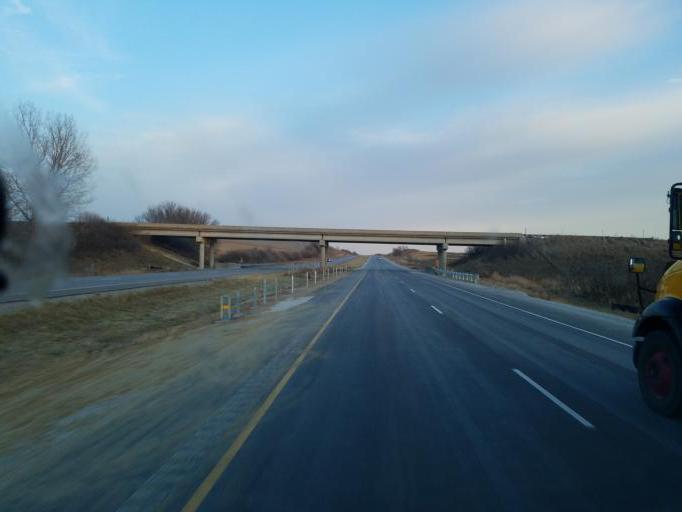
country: US
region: Iowa
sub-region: Harrison County
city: Logan
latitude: 41.4981
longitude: -95.6710
